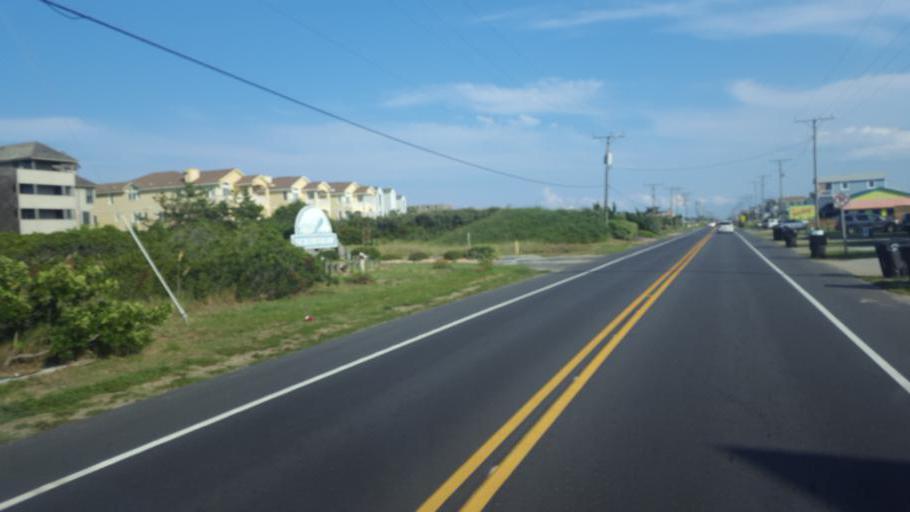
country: US
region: North Carolina
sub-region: Dare County
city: Kill Devil Hills
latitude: 36.0314
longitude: -75.6677
